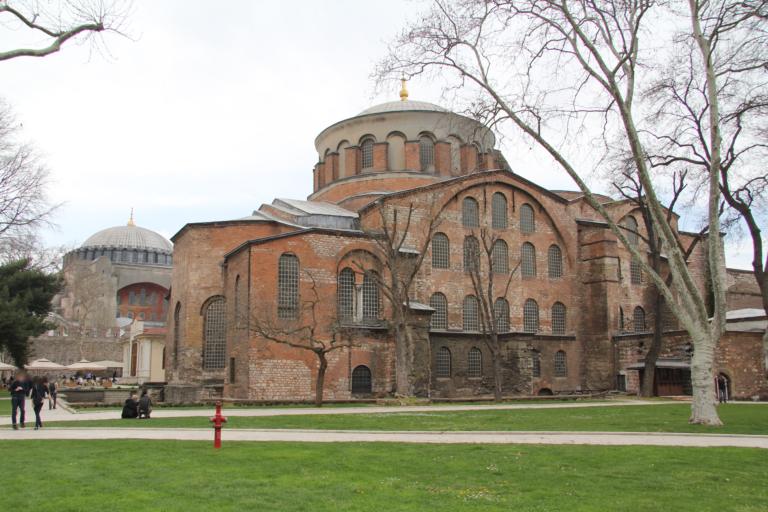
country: TR
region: Istanbul
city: Eminoenue
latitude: 41.0097
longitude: 28.9811
